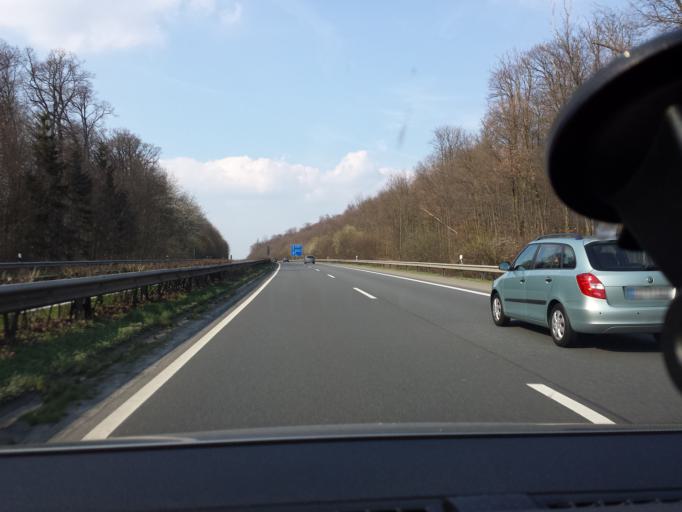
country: DE
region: Lower Saxony
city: Wolfenbuettel
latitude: 52.1443
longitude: 10.4935
